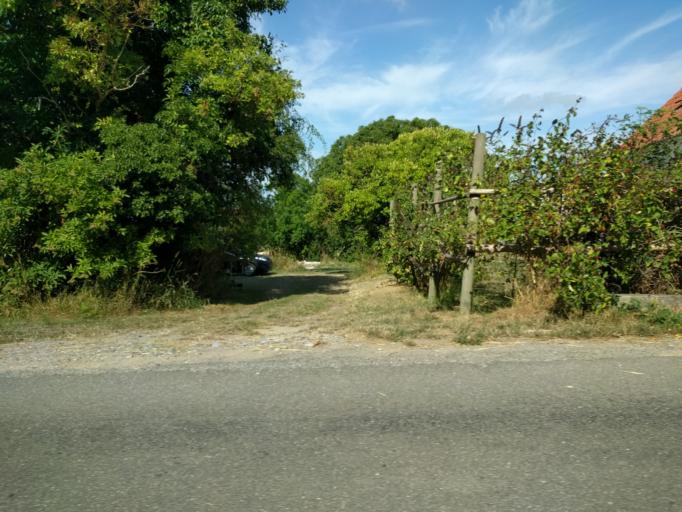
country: DK
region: Zealand
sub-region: Vordingborg Kommune
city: Stege
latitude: 54.9660
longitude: 12.2951
